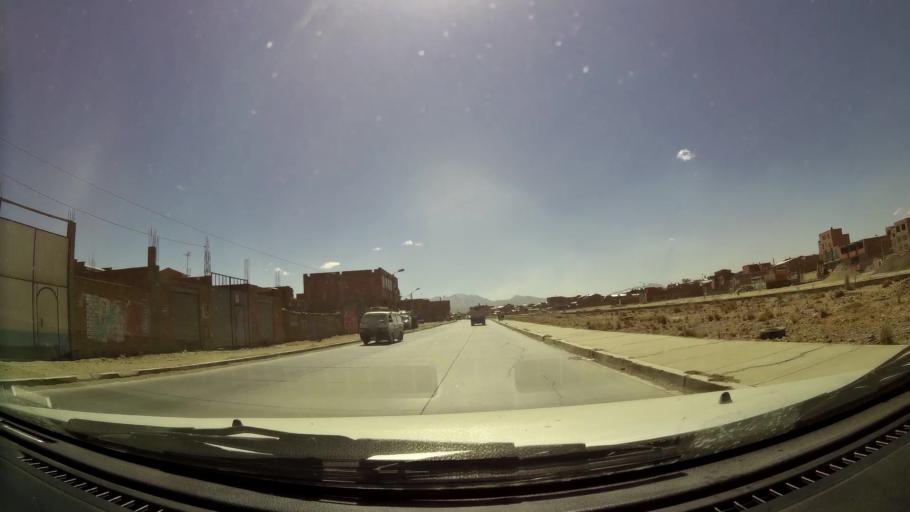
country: BO
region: La Paz
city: La Paz
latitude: -16.5045
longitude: -68.2107
